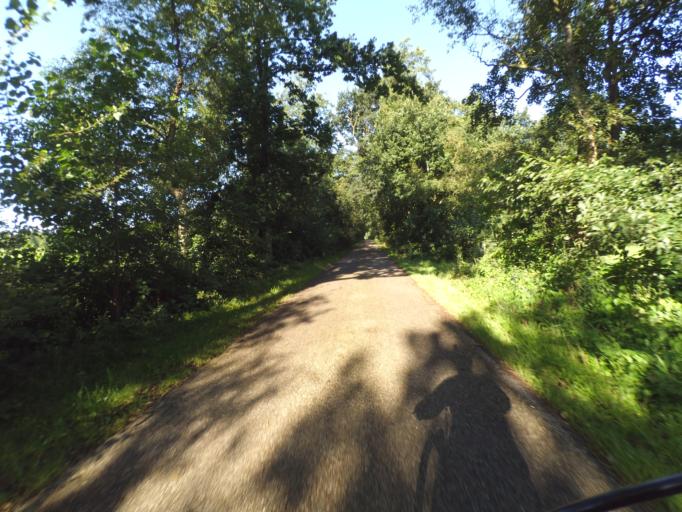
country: NL
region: Friesland
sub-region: Gemeente Achtkarspelen
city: Buitenpost
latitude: 53.2657
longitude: 6.1419
